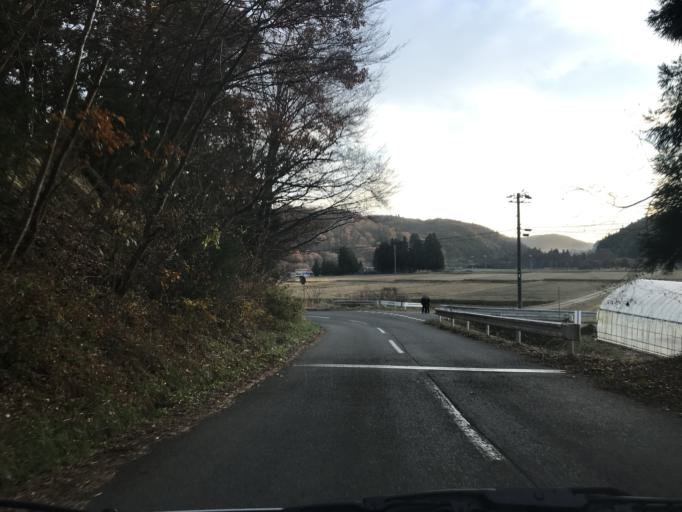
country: JP
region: Iwate
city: Ichinoseki
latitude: 38.9133
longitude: 141.0506
